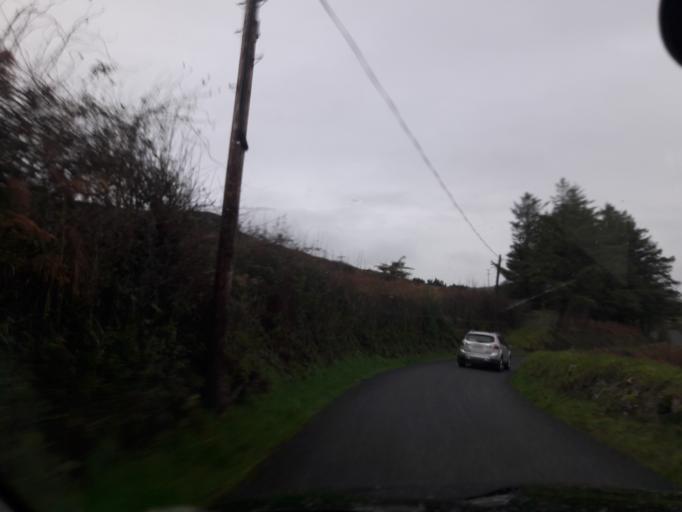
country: IE
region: Ulster
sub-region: County Donegal
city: Buncrana
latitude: 55.2366
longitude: -7.6186
